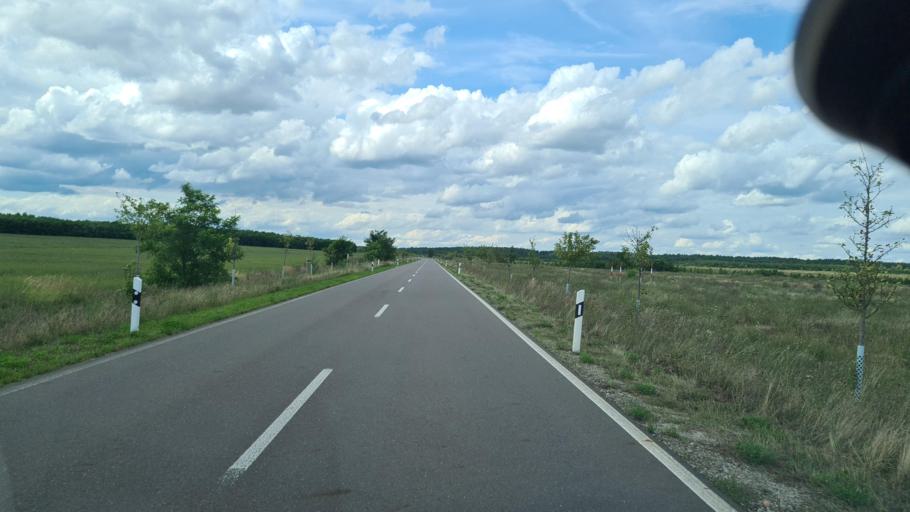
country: DE
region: Brandenburg
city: Drebkau
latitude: 51.6079
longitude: 14.2728
